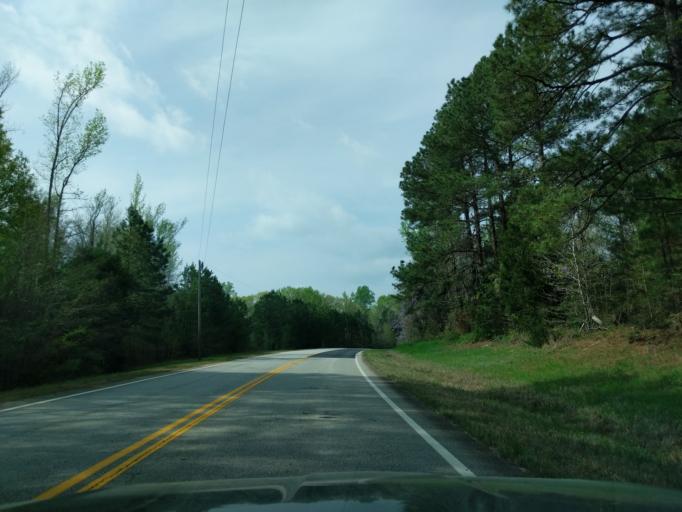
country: US
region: Georgia
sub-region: Lincoln County
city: Lincolnton
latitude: 33.7588
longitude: -82.3795
